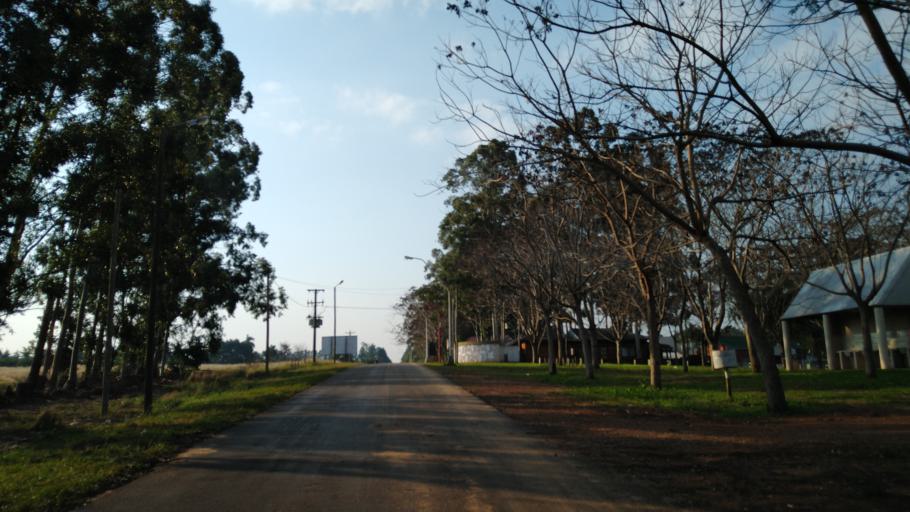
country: AR
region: Entre Rios
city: Santa Ana
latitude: -30.9132
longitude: -57.9269
